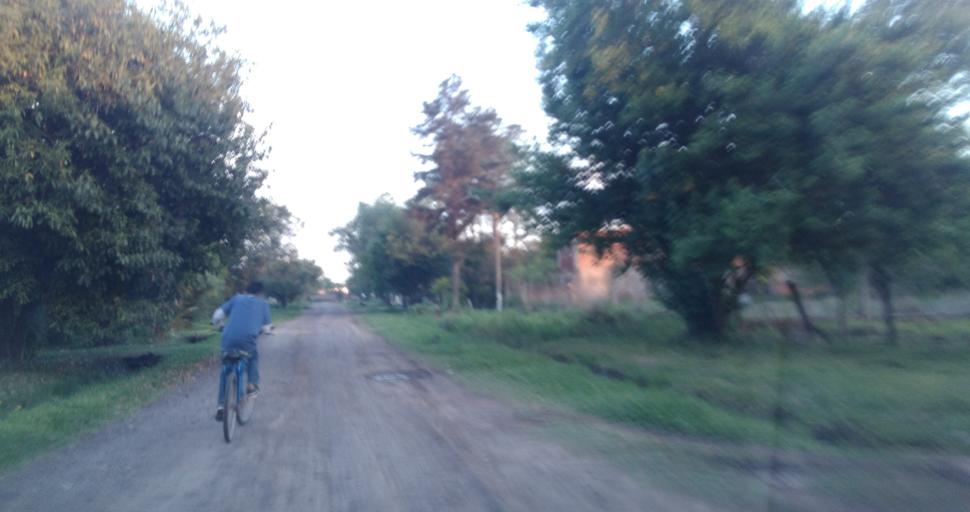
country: AR
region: Chaco
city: Fontana
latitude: -27.4019
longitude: -59.0025
